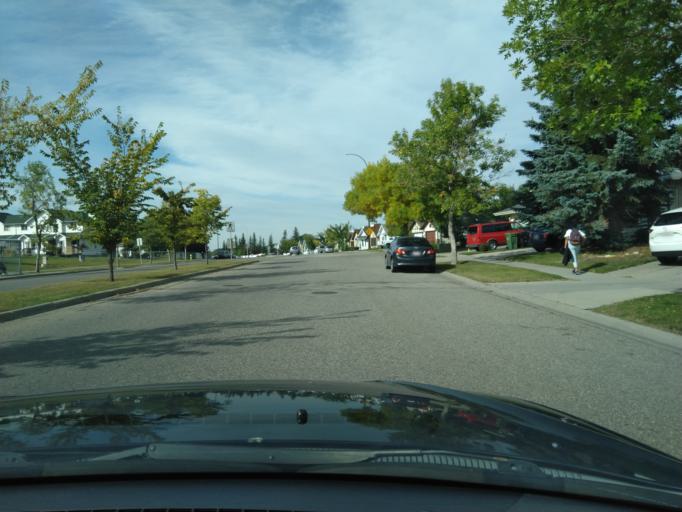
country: CA
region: Alberta
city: Calgary
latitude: 51.1362
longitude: -114.0908
